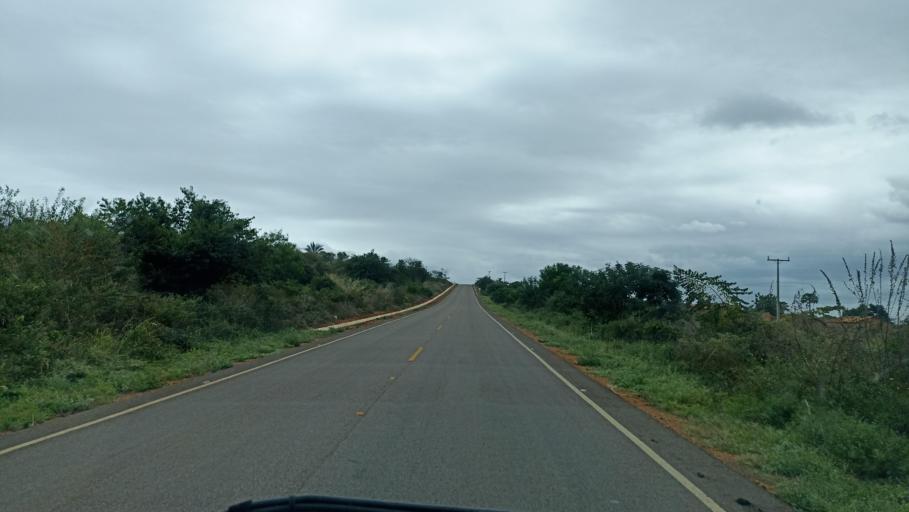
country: BR
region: Bahia
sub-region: Andarai
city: Vera Cruz
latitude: -12.9984
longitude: -40.9933
